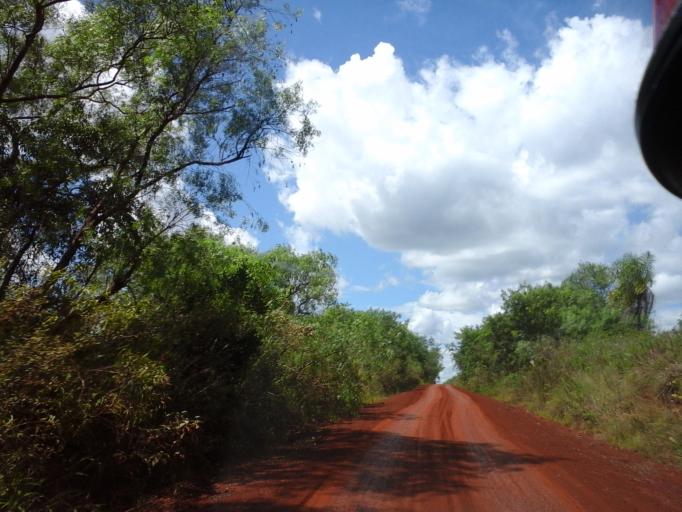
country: AR
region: Misiones
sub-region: Departamento de Apostoles
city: Apostoles
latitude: -27.9781
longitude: -55.7756
